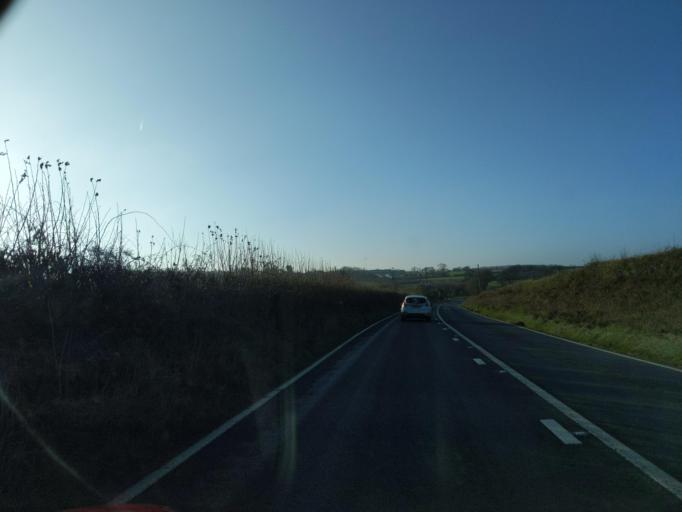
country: GB
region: England
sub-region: Cornwall
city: Liskeard
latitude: 50.4506
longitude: -4.5452
